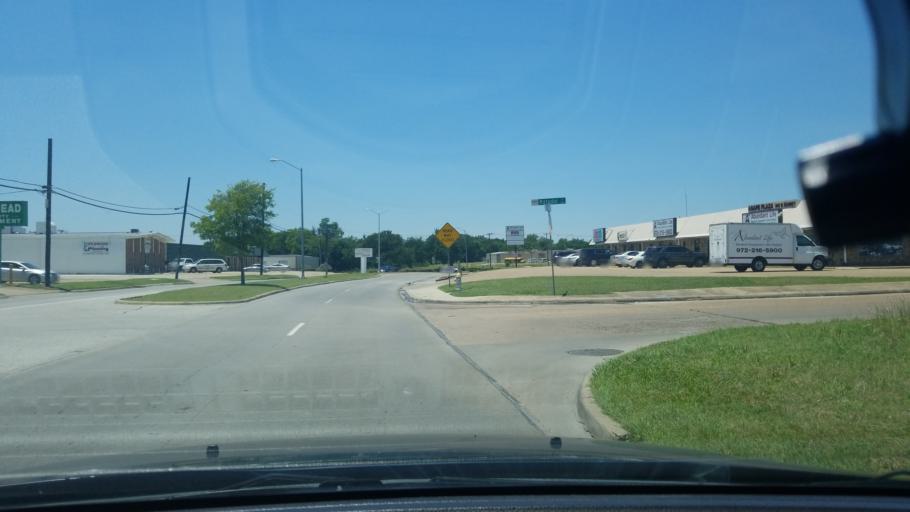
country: US
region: Texas
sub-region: Dallas County
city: Mesquite
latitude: 32.7709
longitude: -96.6109
